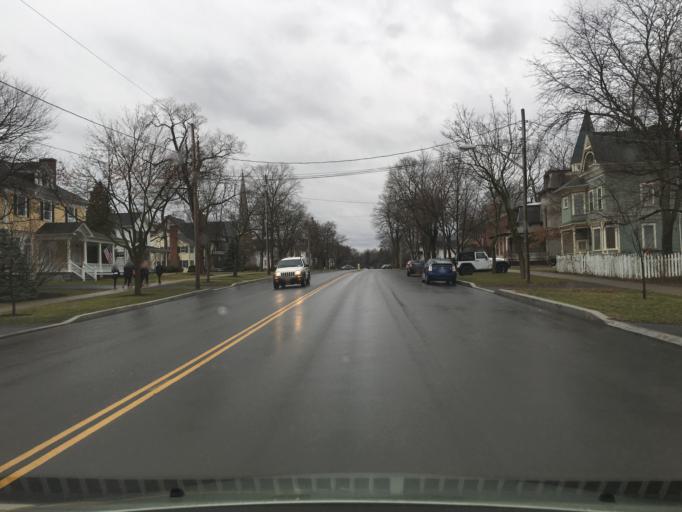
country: US
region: New York
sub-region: Livingston County
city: Geneseo
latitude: 42.7994
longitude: -77.8161
